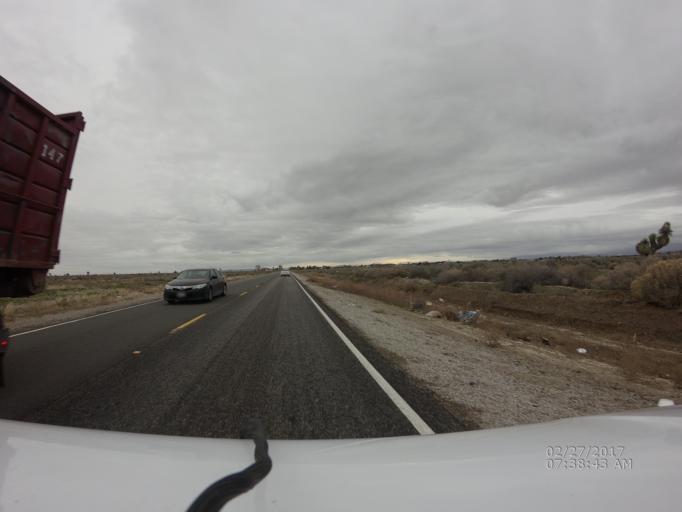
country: US
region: California
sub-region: Los Angeles County
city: Lancaster
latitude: 34.7189
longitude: -118.0853
